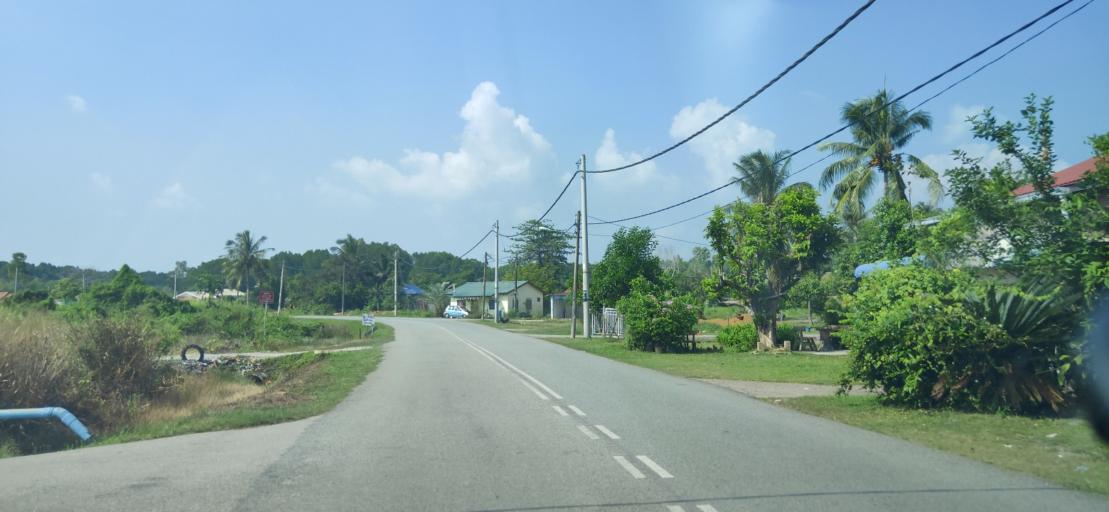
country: MY
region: Kedah
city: Sungai Petani
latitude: 5.6510
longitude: 100.4627
